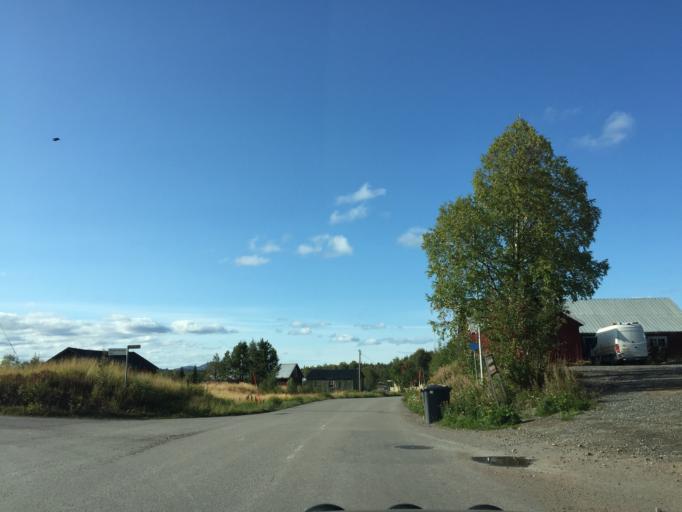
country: SE
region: Norrbotten
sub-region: Gallivare Kommun
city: Malmberget
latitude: 67.6463
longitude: 21.0497
